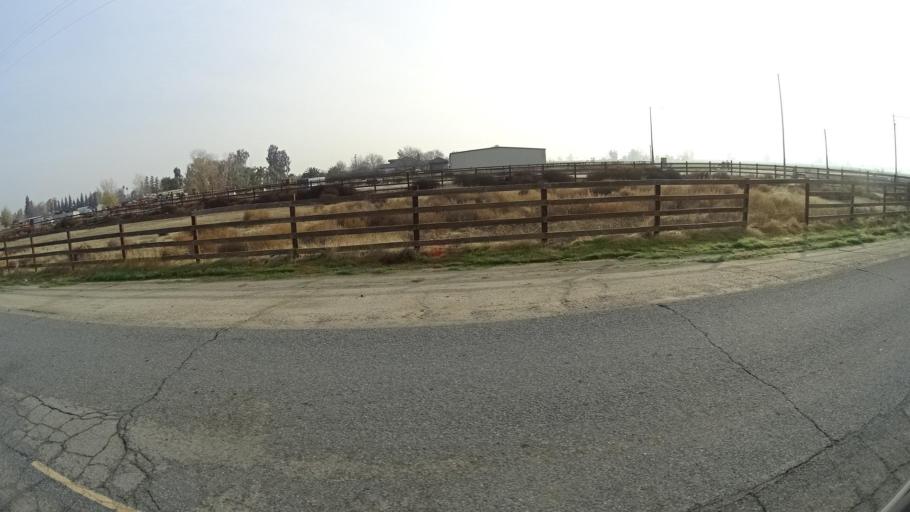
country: US
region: California
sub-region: Kern County
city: Greenfield
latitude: 35.2199
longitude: -119.0215
